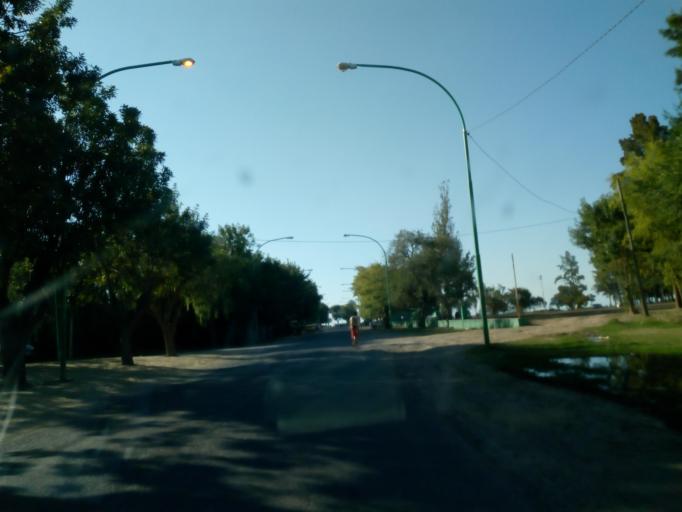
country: AR
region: Buenos Aires
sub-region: Partido de Ensenada
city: Ensenada
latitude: -34.8094
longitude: -57.9816
